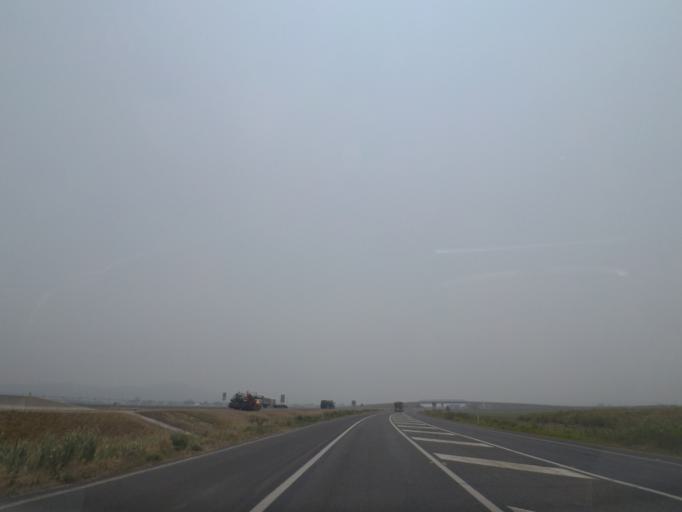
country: AU
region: New South Wales
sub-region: Clarence Valley
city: Maclean
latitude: -29.3977
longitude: 153.2395
